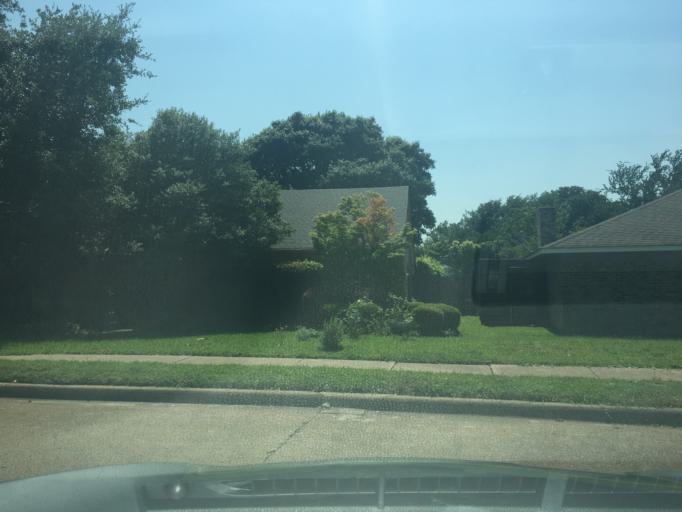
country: US
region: Texas
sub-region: Dallas County
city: Richardson
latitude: 32.9250
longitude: -96.7092
